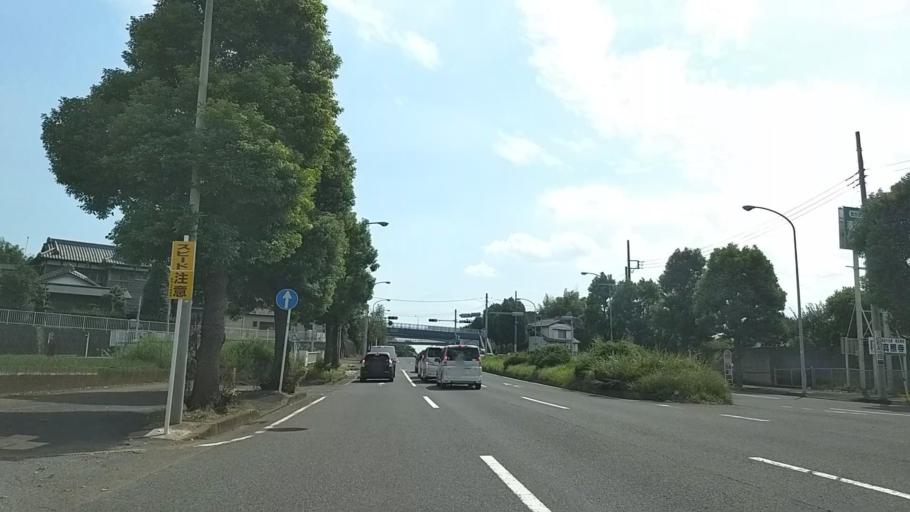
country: JP
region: Kanagawa
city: Yokohama
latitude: 35.5285
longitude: 139.5927
